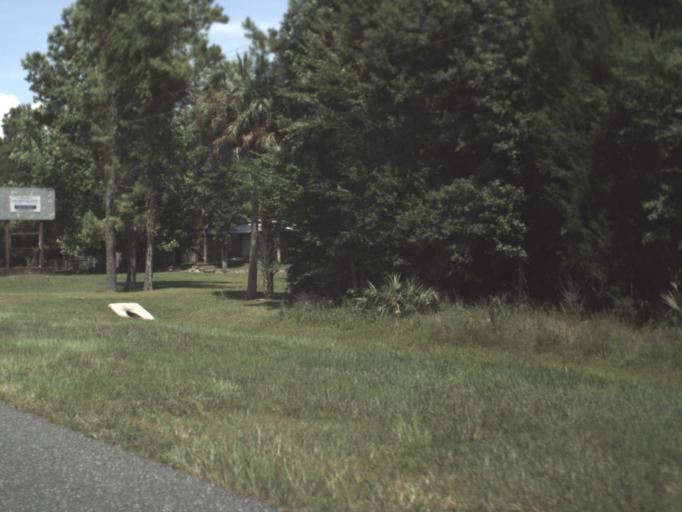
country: US
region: Florida
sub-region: Levy County
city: Inglis
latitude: 29.0514
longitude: -82.6595
